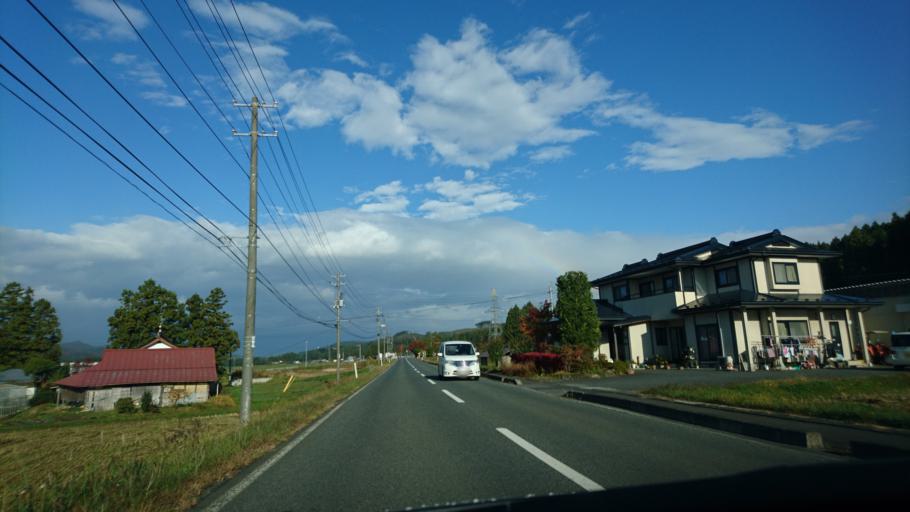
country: JP
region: Iwate
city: Mizusawa
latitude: 39.0265
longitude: 141.0842
